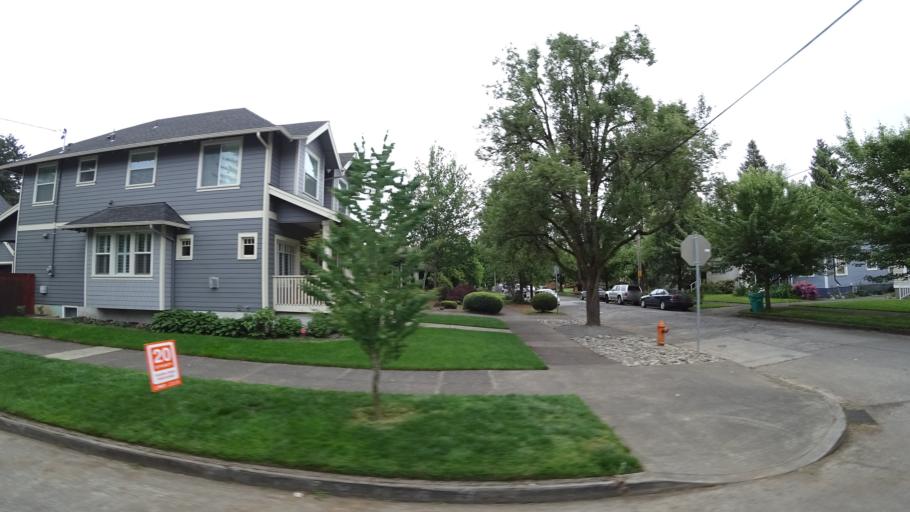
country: US
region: Oregon
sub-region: Multnomah County
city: Portland
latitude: 45.5447
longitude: -122.6286
